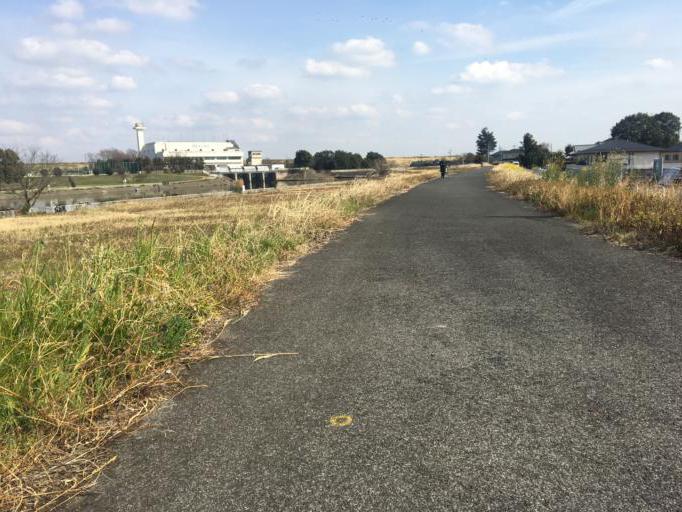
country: JP
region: Saitama
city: Shiki
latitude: 35.8713
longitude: 139.5686
